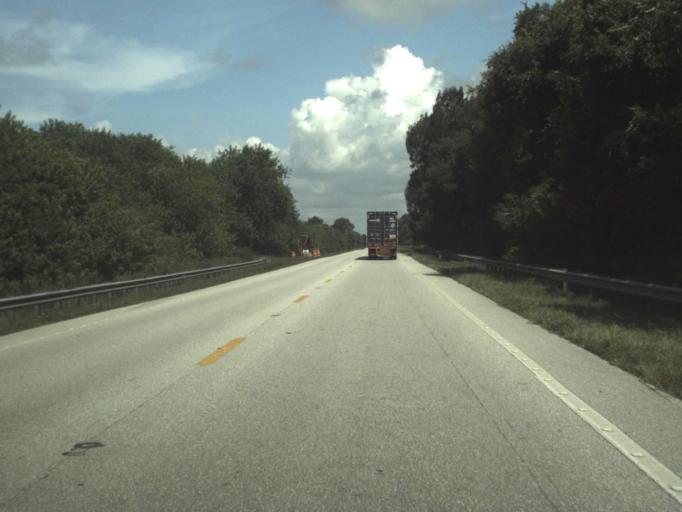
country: US
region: Florida
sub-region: Okeechobee County
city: Taylor Creek
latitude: 27.1478
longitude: -80.6604
